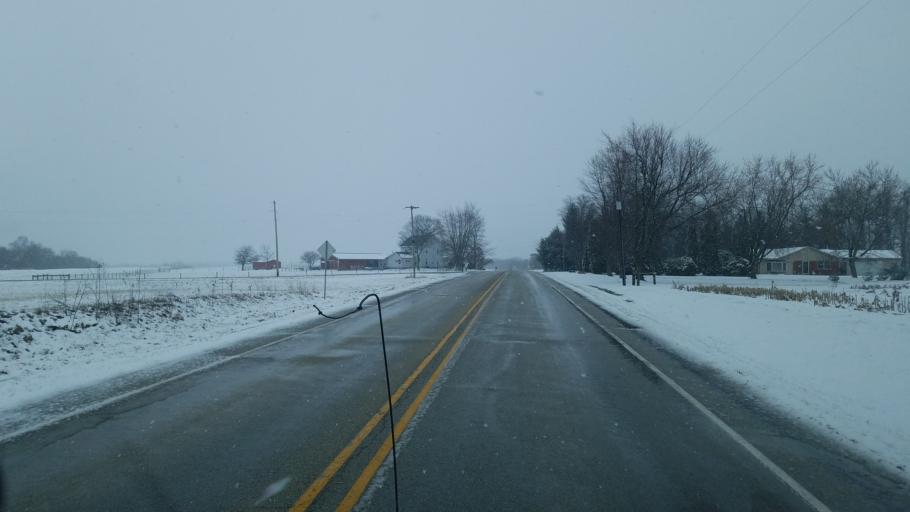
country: US
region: Indiana
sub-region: Randolph County
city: Lynn
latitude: 39.9655
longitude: -85.0260
